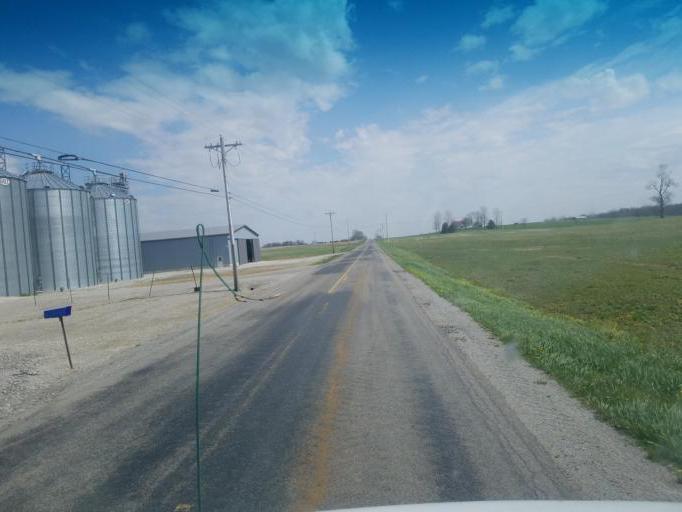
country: US
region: Ohio
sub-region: Hardin County
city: Kenton
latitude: 40.5785
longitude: -83.6851
